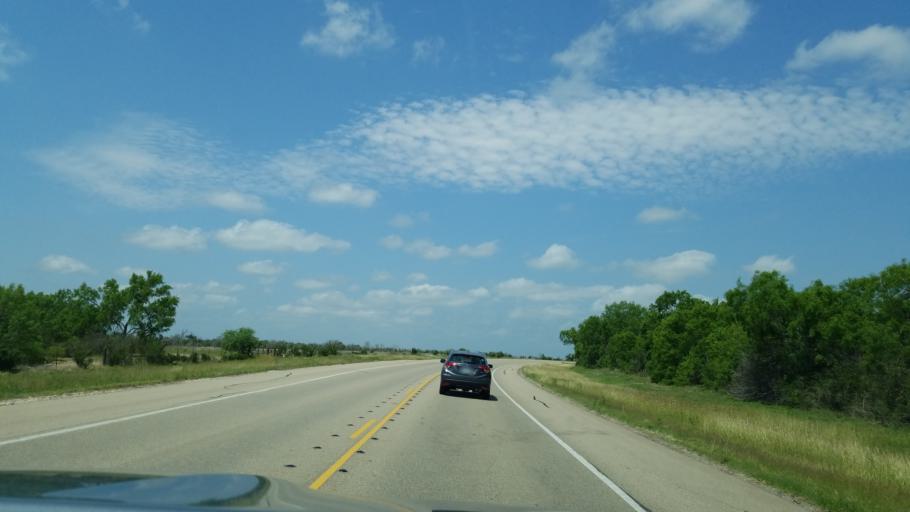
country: US
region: Texas
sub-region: Frio County
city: Pearsall
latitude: 29.0068
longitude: -99.1455
